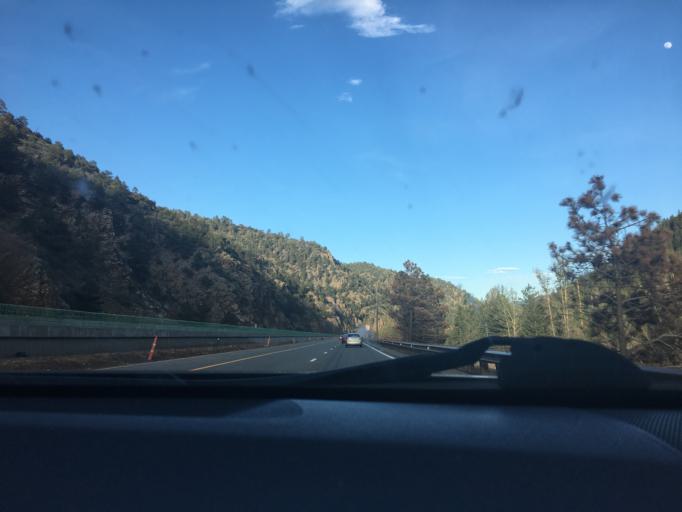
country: US
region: Colorado
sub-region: Clear Creek County
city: Idaho Springs
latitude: 39.7638
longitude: -105.5860
